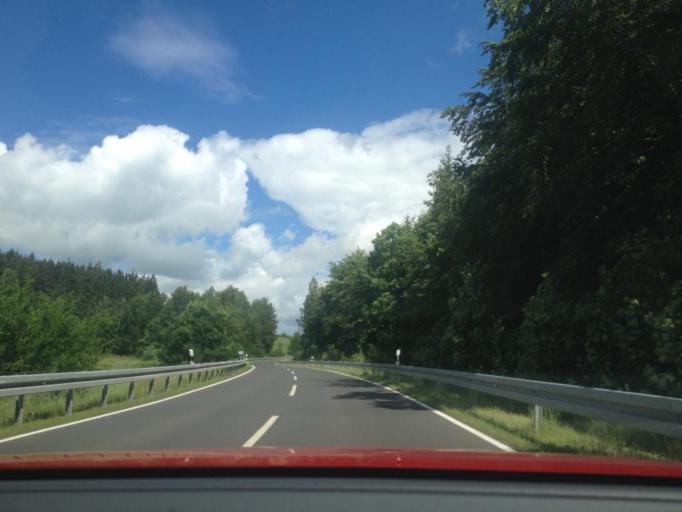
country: DE
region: Bavaria
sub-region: Upper Franconia
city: Arzberg
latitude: 50.0406
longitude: 12.2004
